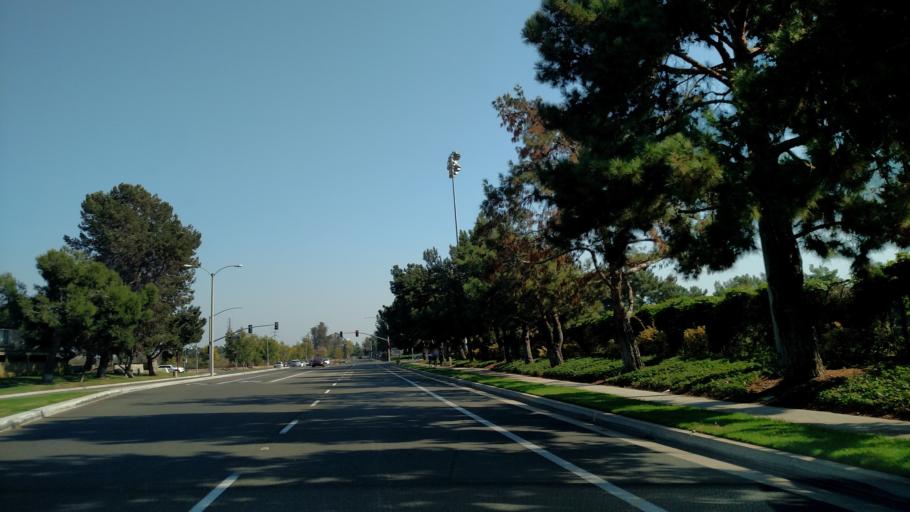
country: US
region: California
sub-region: Orange County
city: Irvine
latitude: 33.6742
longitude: -117.7861
